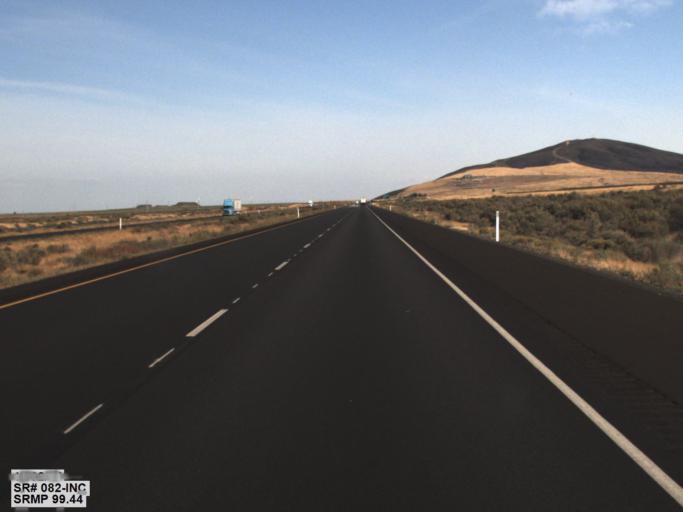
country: US
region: Washington
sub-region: Benton County
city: Benton City
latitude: 46.2604
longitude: -119.4179
